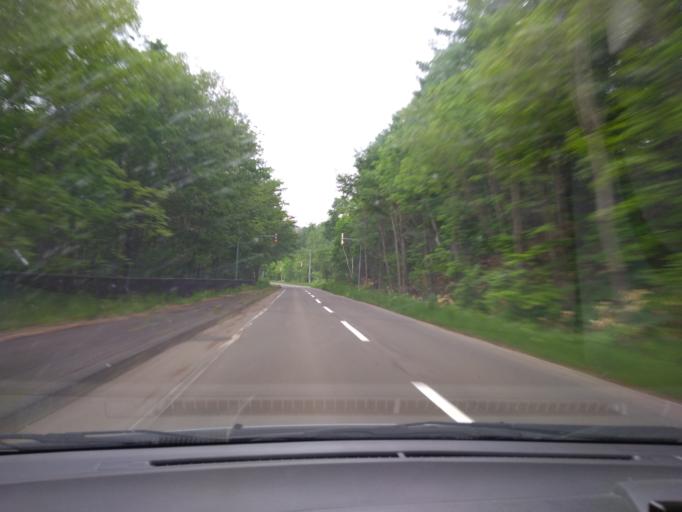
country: JP
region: Hokkaido
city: Shimo-furano
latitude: 43.1756
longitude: 142.5463
